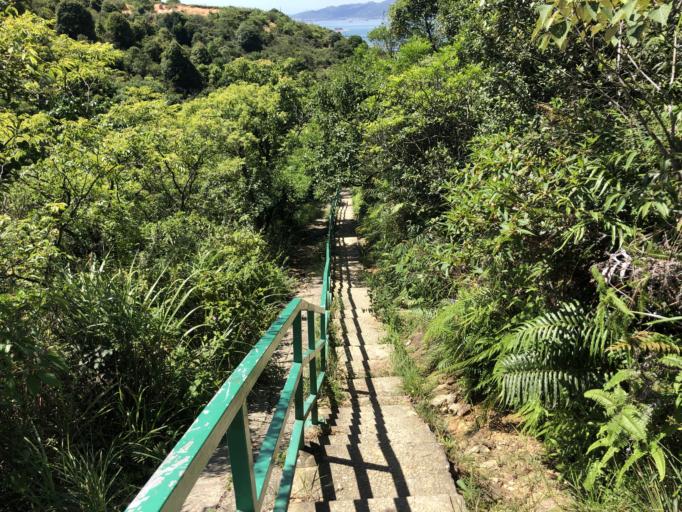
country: HK
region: Tuen Mun
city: Tuen Mun
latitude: 22.2822
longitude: 113.9833
